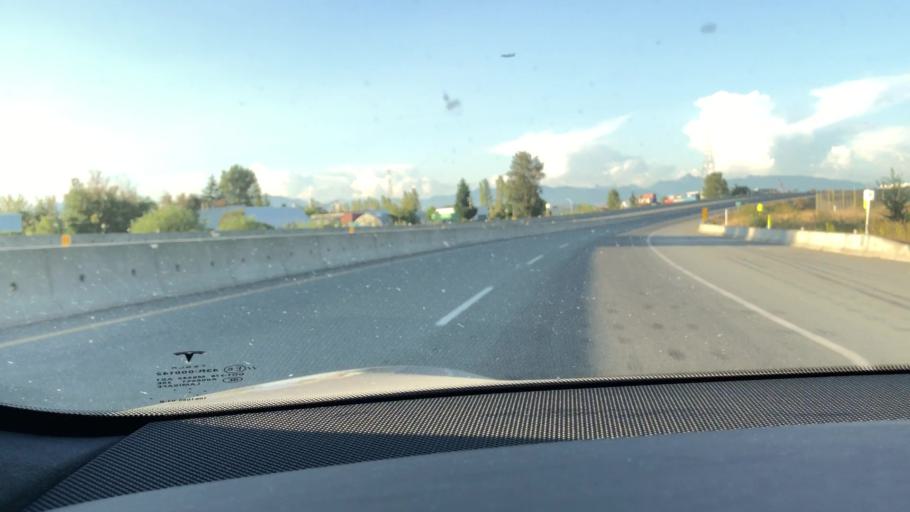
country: CA
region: British Columbia
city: Delta
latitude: 49.1437
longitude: -122.9923
